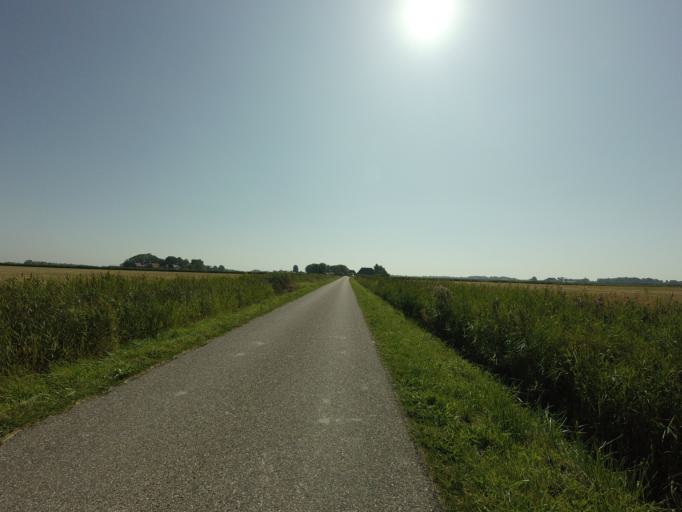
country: NL
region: Friesland
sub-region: Gemeente Dongeradeel
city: Holwerd
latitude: 53.3692
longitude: 5.9200
